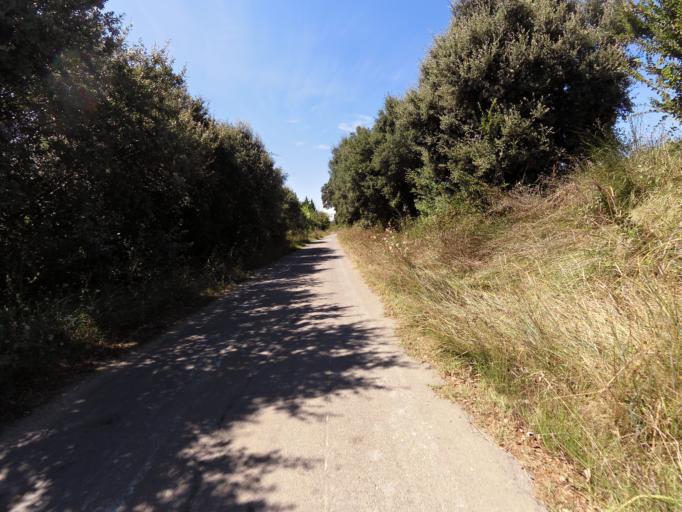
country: FR
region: Languedoc-Roussillon
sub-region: Departement du Gard
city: Aubais
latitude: 43.7539
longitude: 4.1280
